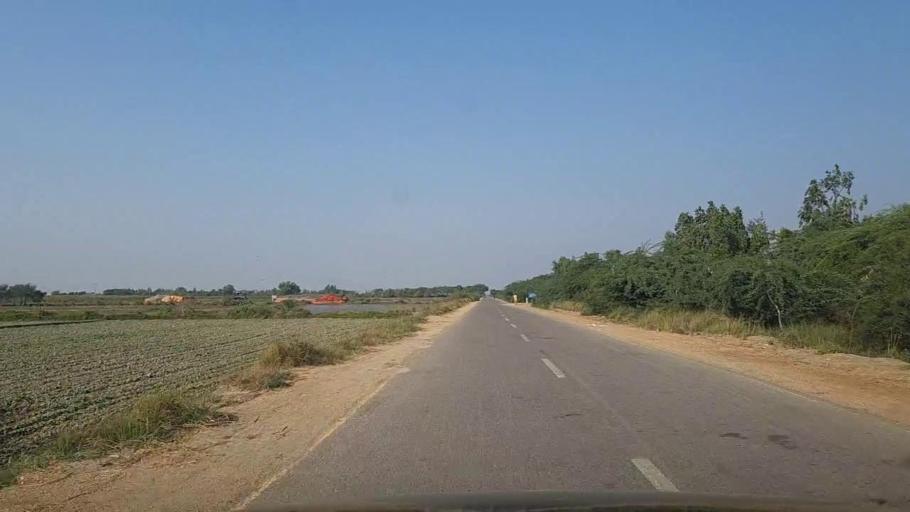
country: PK
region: Sindh
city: Thatta
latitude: 24.6178
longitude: 68.0516
